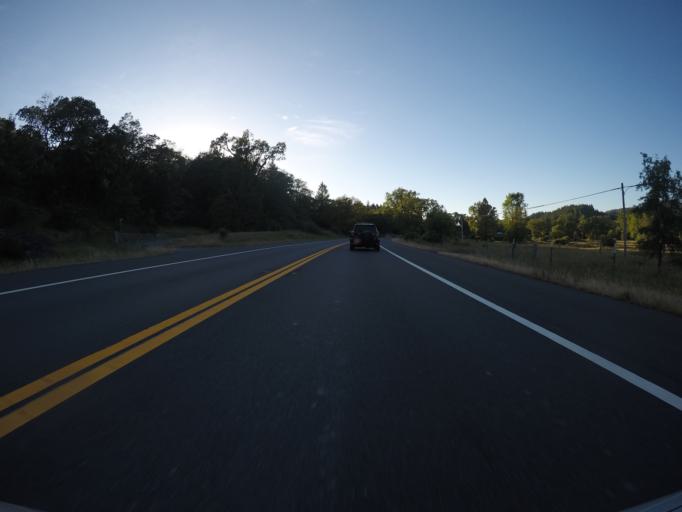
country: US
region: California
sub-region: Mendocino County
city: Laytonville
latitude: 39.6413
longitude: -123.4723
